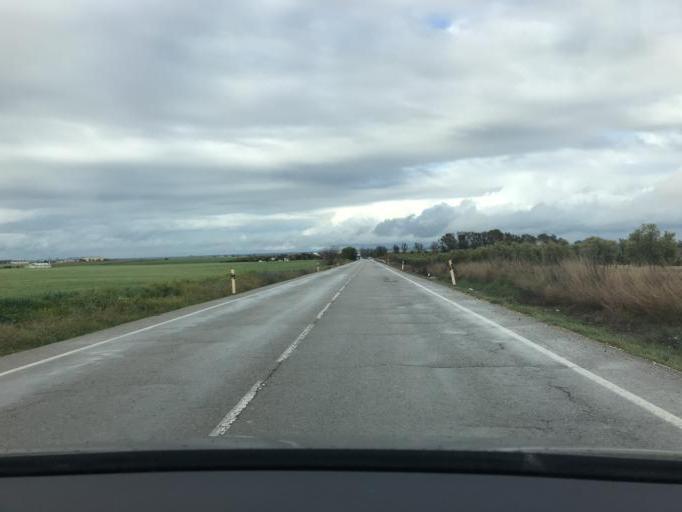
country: ES
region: Andalusia
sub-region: Provincia de Sevilla
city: Ecija
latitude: 37.5081
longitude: -5.1248
